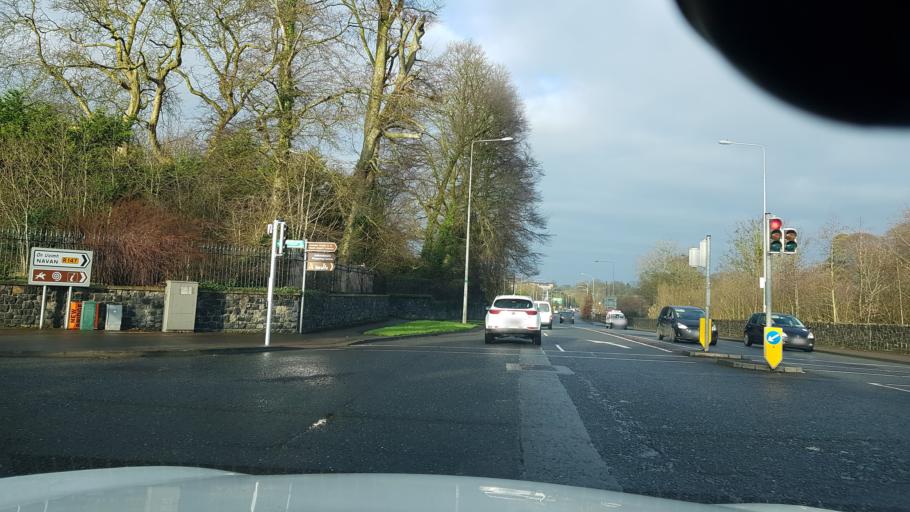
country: IE
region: Leinster
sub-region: An Mhi
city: Navan
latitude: 53.6421
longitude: -6.6711
